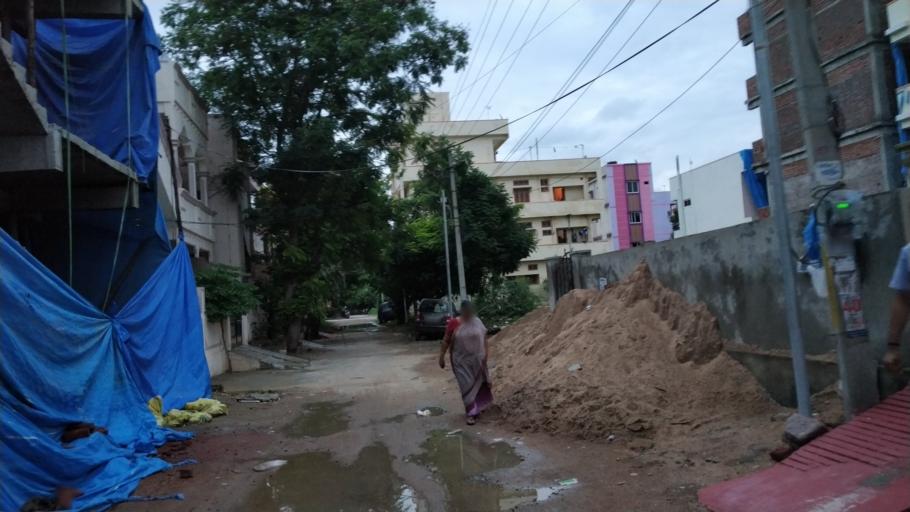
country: IN
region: Telangana
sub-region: Medak
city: Serilingampalle
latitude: 17.5093
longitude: 78.3065
